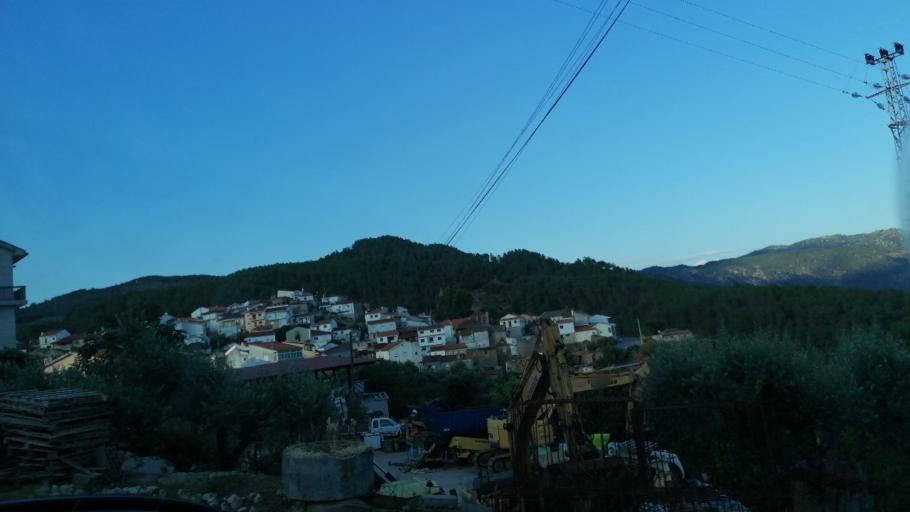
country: PT
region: Viseu
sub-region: Sao Joao da Pesqueira
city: Sao Joao da Pesqueira
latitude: 41.2470
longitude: -7.4326
